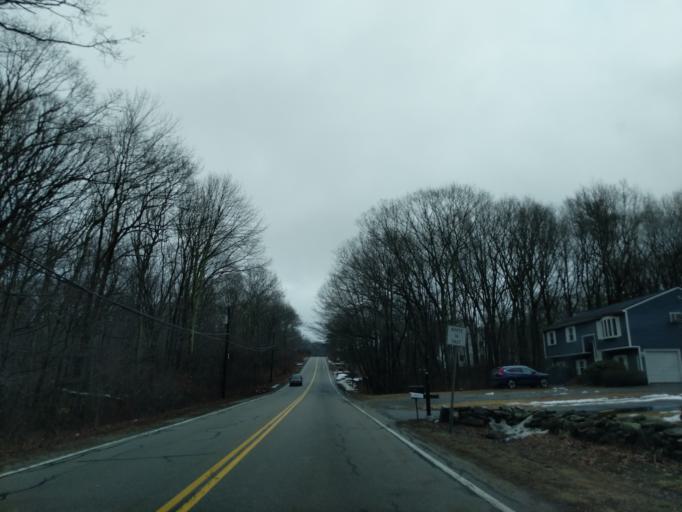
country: US
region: Massachusetts
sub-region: Worcester County
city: Webster
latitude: 42.0583
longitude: -71.8250
